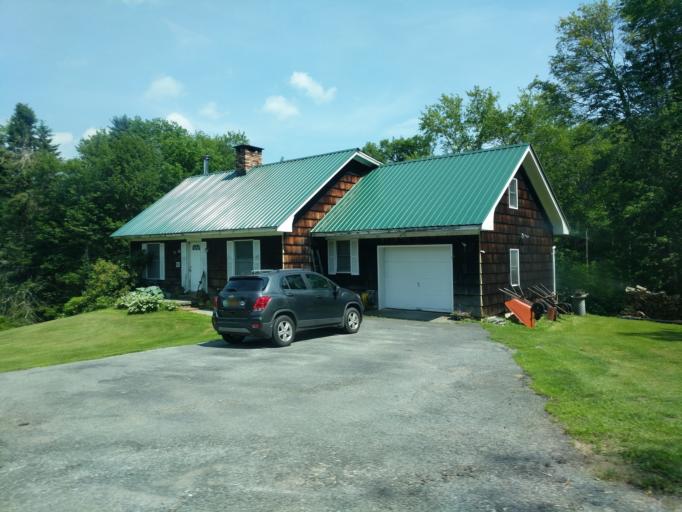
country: US
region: New York
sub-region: Sullivan County
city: Livingston Manor
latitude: 41.9119
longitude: -74.9404
